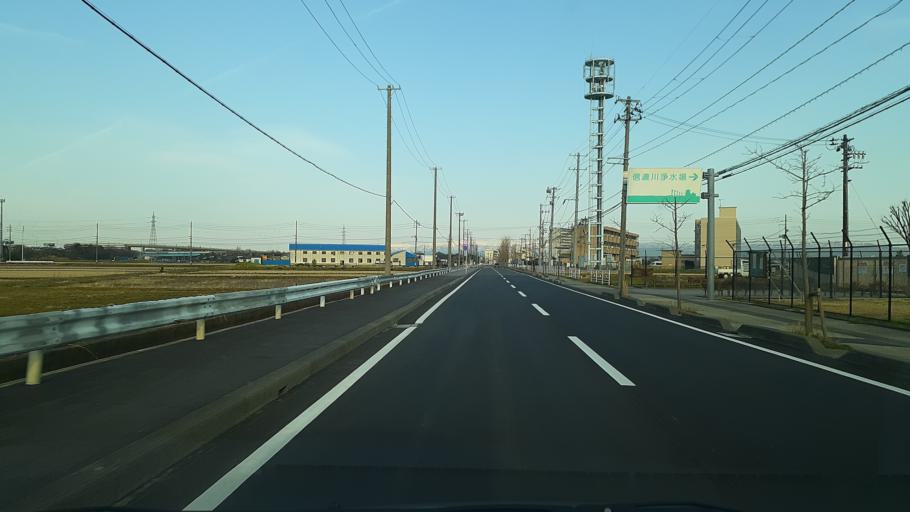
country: JP
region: Niigata
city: Niigata-shi
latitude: 37.8678
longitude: 139.0310
